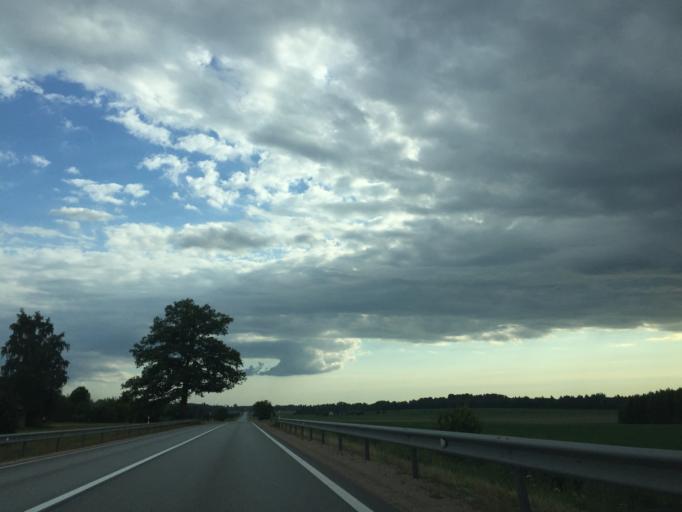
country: LV
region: Sigulda
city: Sigulda
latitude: 57.2579
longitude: 24.8662
